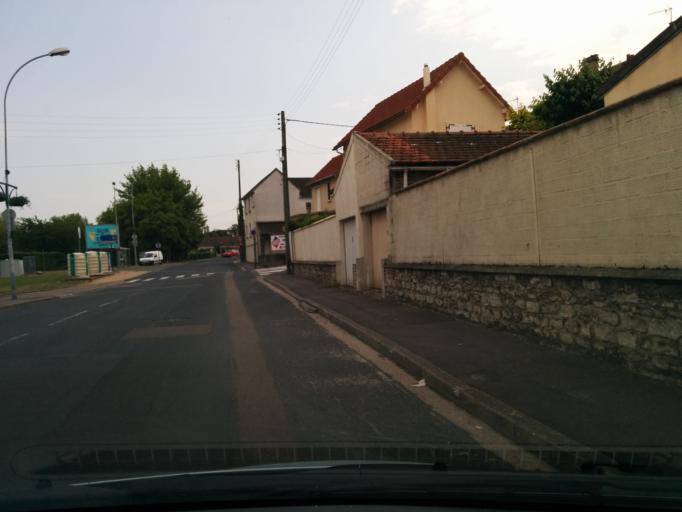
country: FR
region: Ile-de-France
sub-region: Departement des Yvelines
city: Mantes-la-Jolie
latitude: 48.9970
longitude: 1.7073
